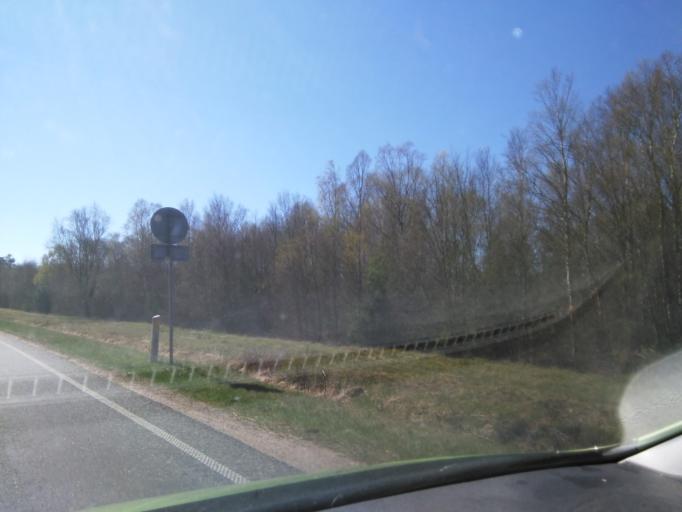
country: DK
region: South Denmark
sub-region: Varde Kommune
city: Oksbol
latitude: 55.6036
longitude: 8.2251
